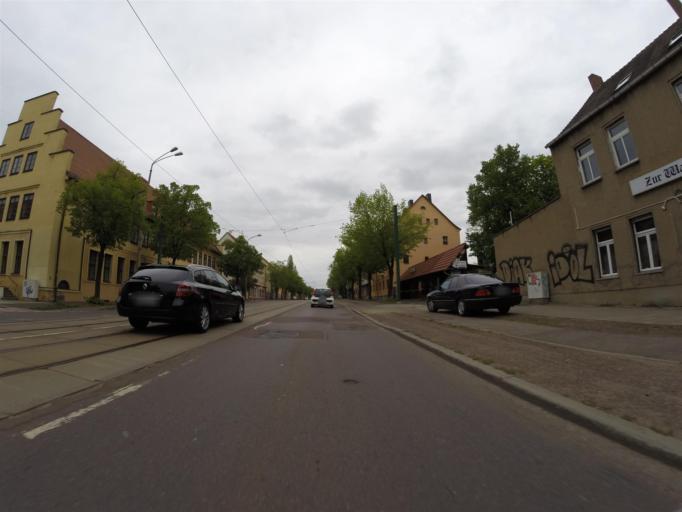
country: DE
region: Saxony-Anhalt
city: Schkopau
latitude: 51.4293
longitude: 11.9843
